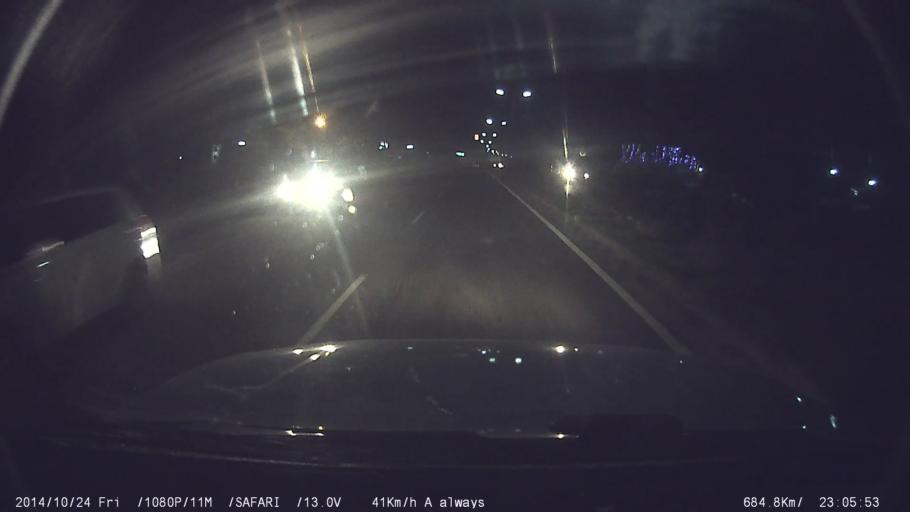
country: IN
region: Tamil Nadu
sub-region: Salem
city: Salem
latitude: 11.6337
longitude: 78.1257
